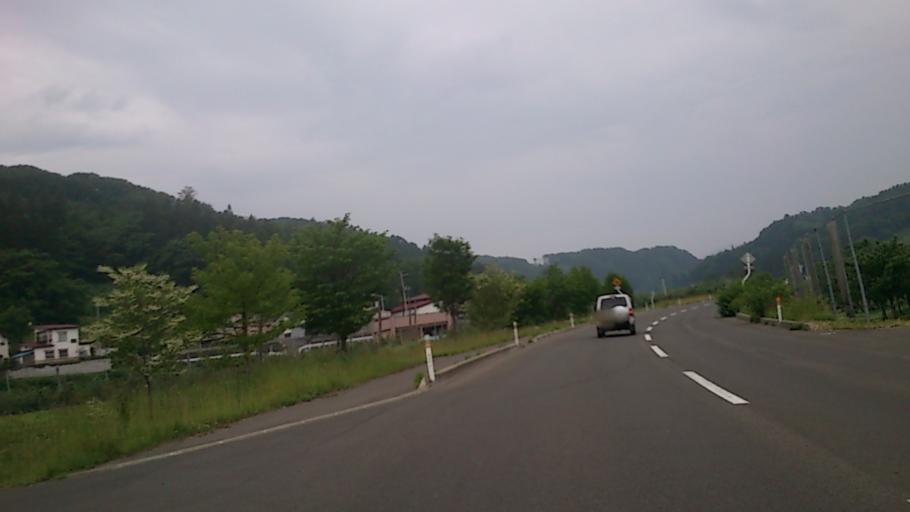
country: JP
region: Aomori
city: Hirosaki
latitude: 40.5874
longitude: 140.3852
